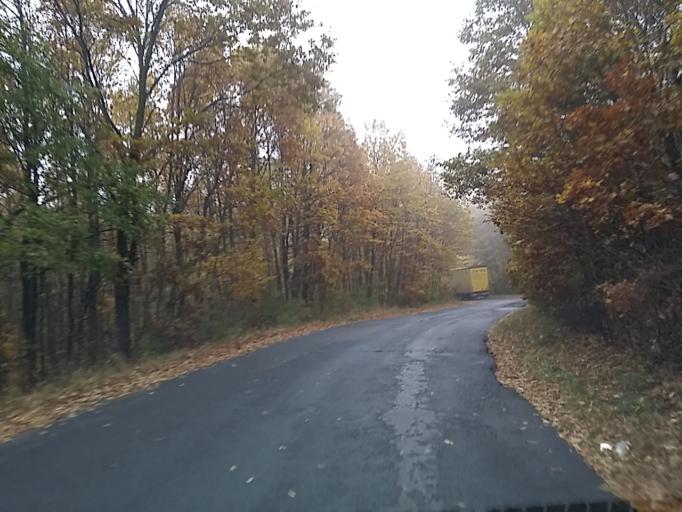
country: HU
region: Heves
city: Gyongyossolymos
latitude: 47.8099
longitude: 19.9697
